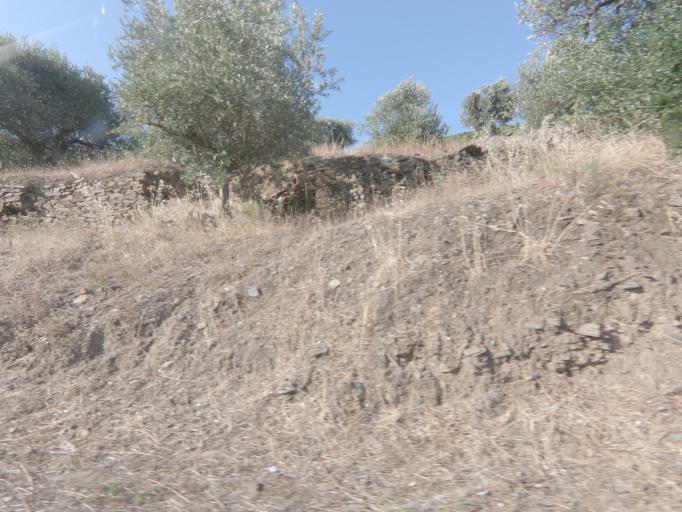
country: PT
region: Viseu
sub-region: Tabuaco
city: Tabuaco
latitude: 41.1750
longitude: -7.5662
